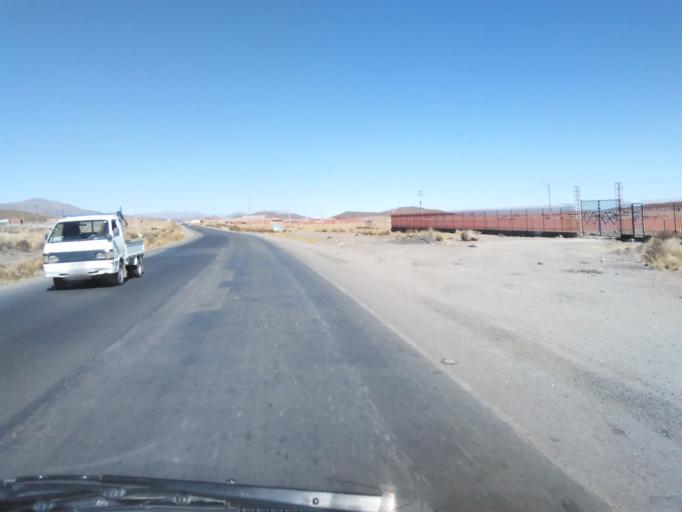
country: BO
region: Oruro
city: Oruro
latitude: -17.9883
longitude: -67.0488
